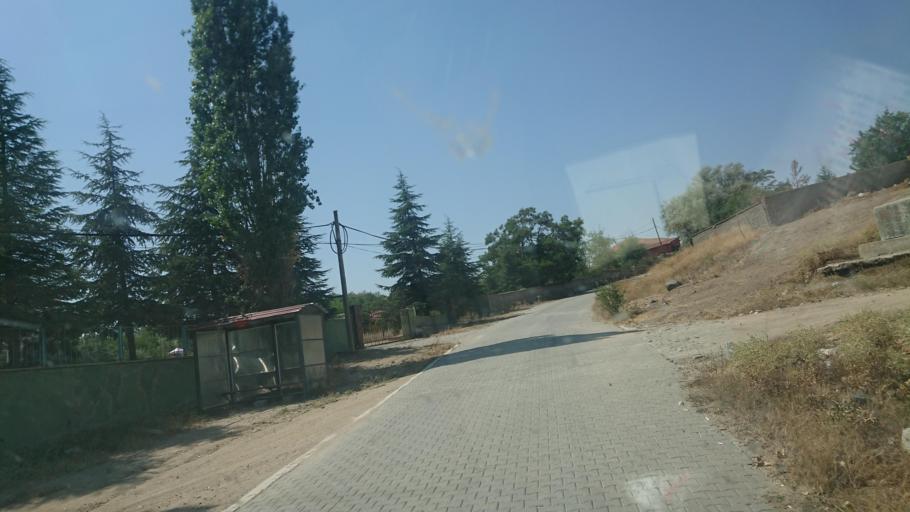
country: TR
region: Aksaray
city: Agacoren
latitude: 38.8188
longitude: 33.9564
